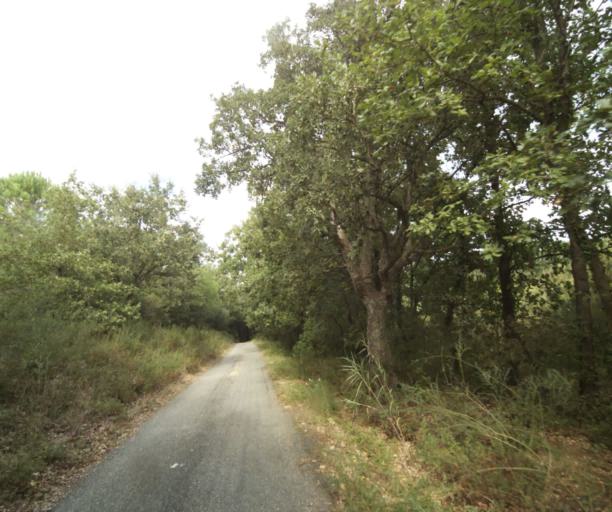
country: FR
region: Languedoc-Roussillon
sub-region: Departement des Pyrenees-Orientales
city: Argelers
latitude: 42.5322
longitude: 3.0223
